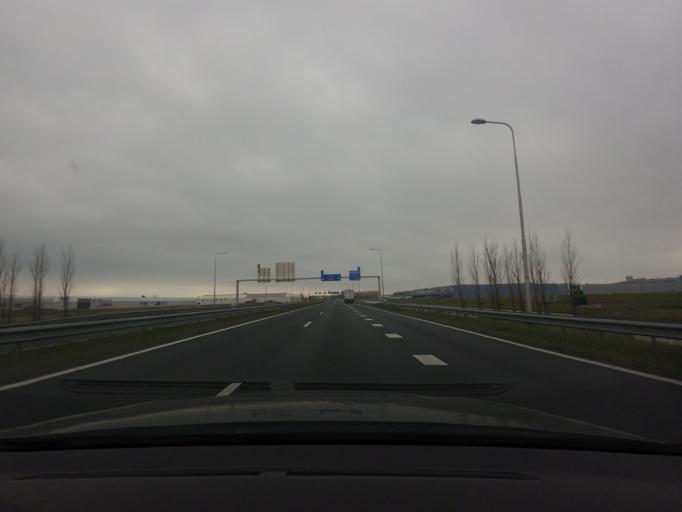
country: NL
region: North Holland
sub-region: Gemeente Aalsmeer
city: Aalsmeer
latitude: 52.2658
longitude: 4.7913
